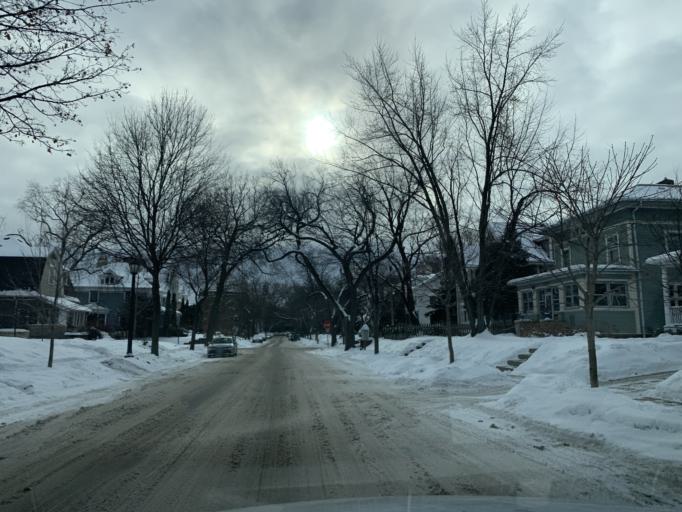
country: US
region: Minnesota
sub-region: Hennepin County
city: Minneapolis
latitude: 44.9579
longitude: -93.2982
